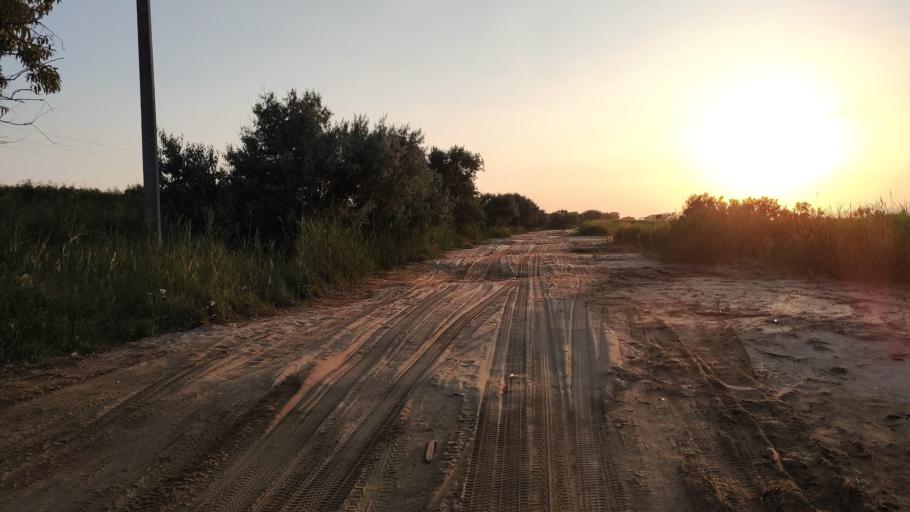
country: RU
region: Krasnodarskiy
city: Blagovetschenskaya
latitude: 45.0684
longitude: 37.0292
